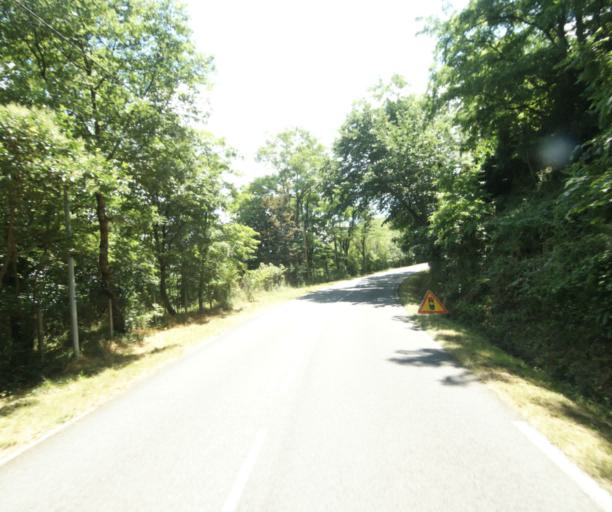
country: FR
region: Midi-Pyrenees
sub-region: Departement de la Haute-Garonne
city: Revel
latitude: 43.4465
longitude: 2.0130
